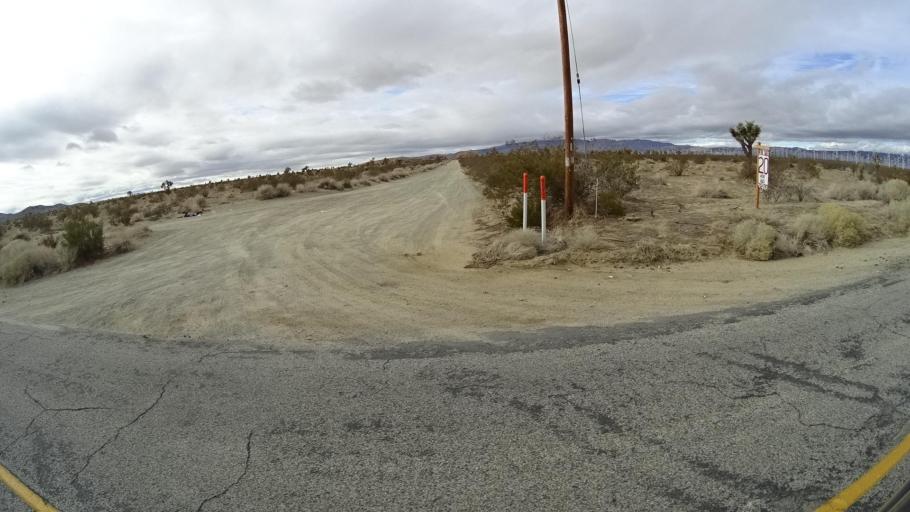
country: US
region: California
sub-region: Kern County
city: Mojave
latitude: 34.9654
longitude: -118.2128
